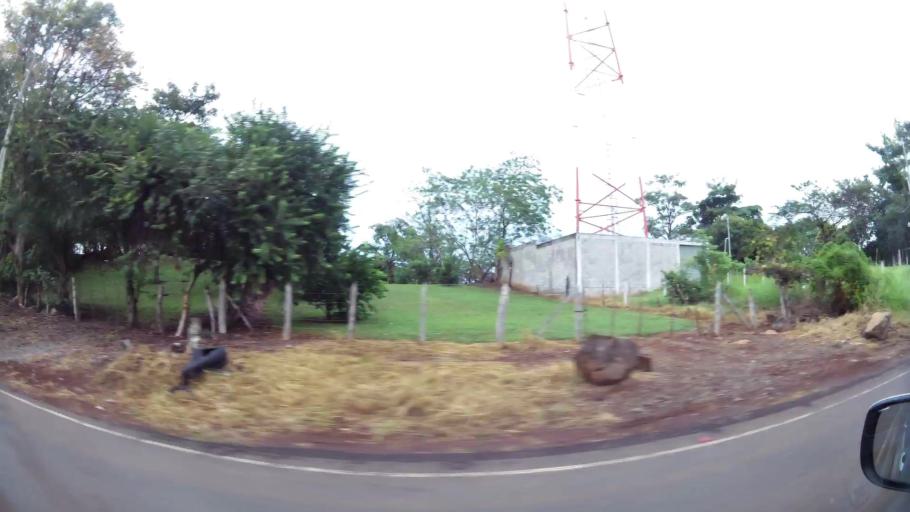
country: CR
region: Puntarenas
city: Esparza
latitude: 9.9786
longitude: -84.6204
